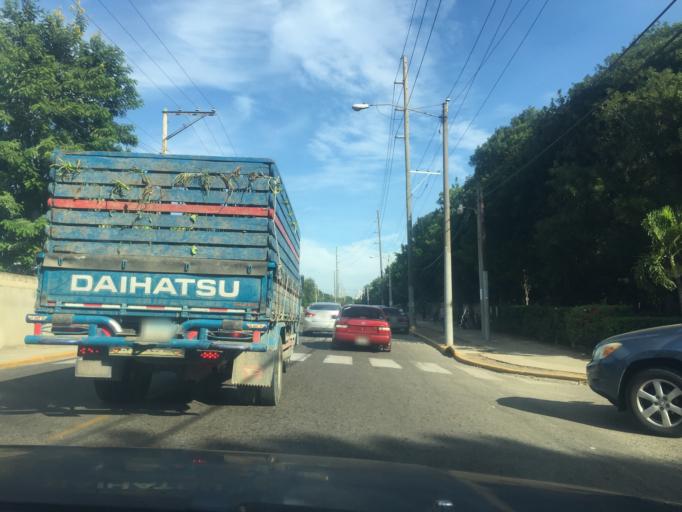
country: DO
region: Santiago
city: Santiago de los Caballeros
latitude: 19.4510
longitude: -70.7449
